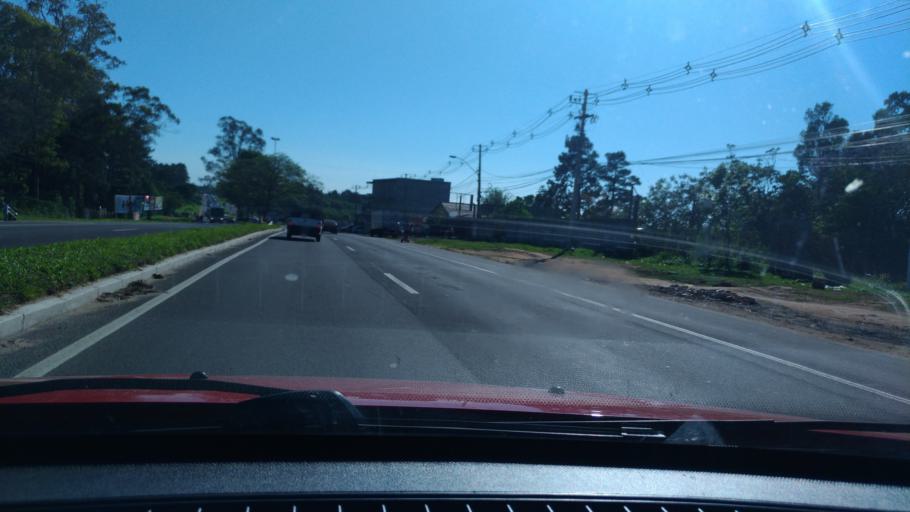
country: BR
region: Rio Grande do Sul
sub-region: Viamao
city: Viamao
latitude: -30.0897
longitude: -51.0615
